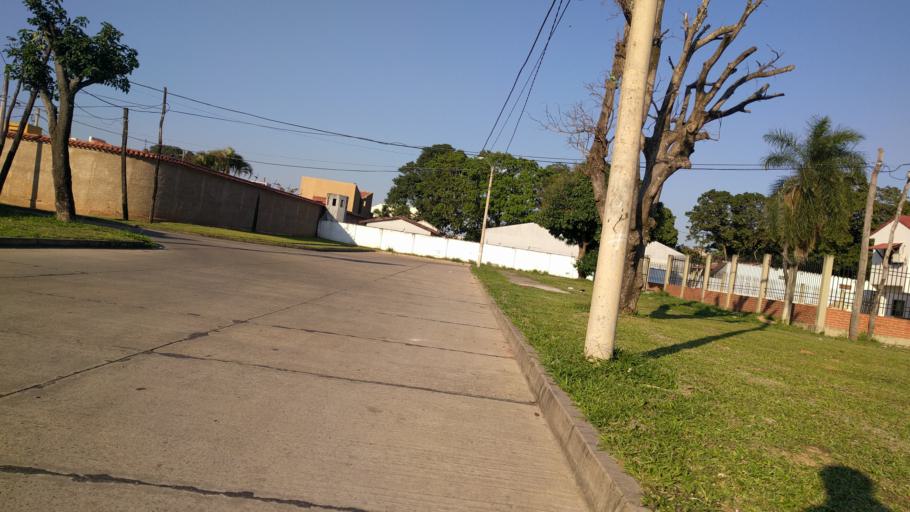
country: BO
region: Santa Cruz
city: Santa Cruz de la Sierra
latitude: -17.8134
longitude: -63.1663
